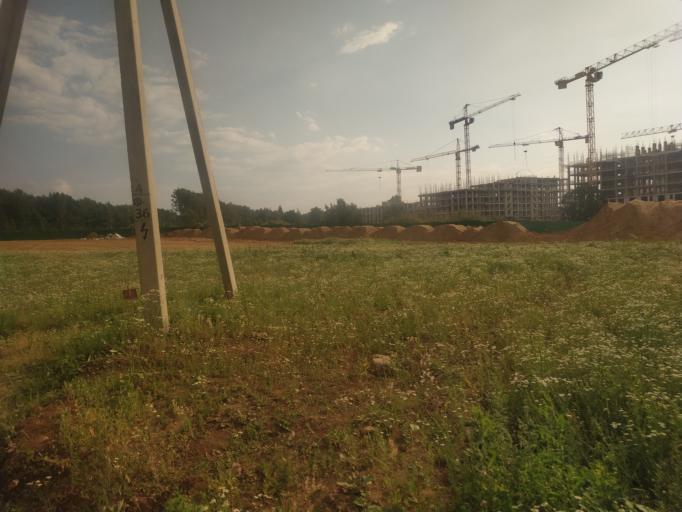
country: RU
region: Moskovskaya
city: Mosrentgen
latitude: 55.5903
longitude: 37.4509
